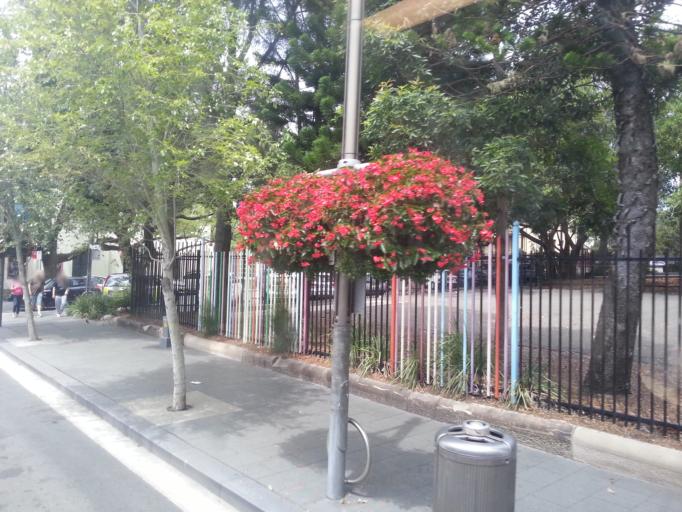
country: AU
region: New South Wales
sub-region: City of Sydney
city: Chippendale
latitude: -33.8834
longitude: 151.1914
